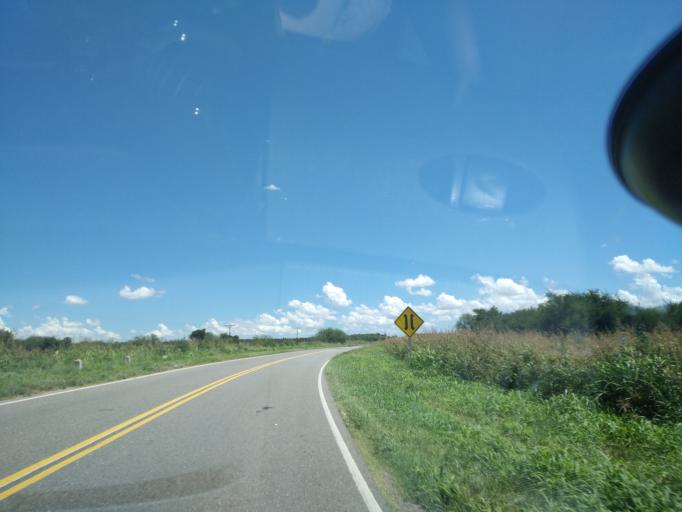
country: AR
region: Cordoba
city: Salsacate
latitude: -31.4193
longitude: -65.0947
